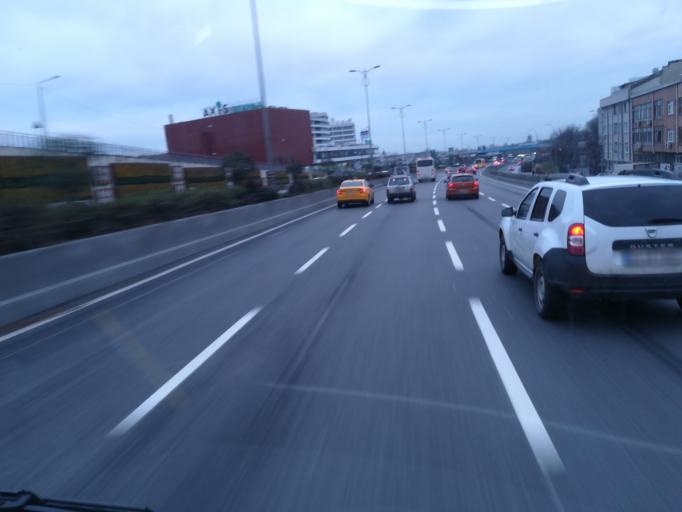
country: TR
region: Istanbul
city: merter keresteciler
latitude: 41.0373
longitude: 28.9174
